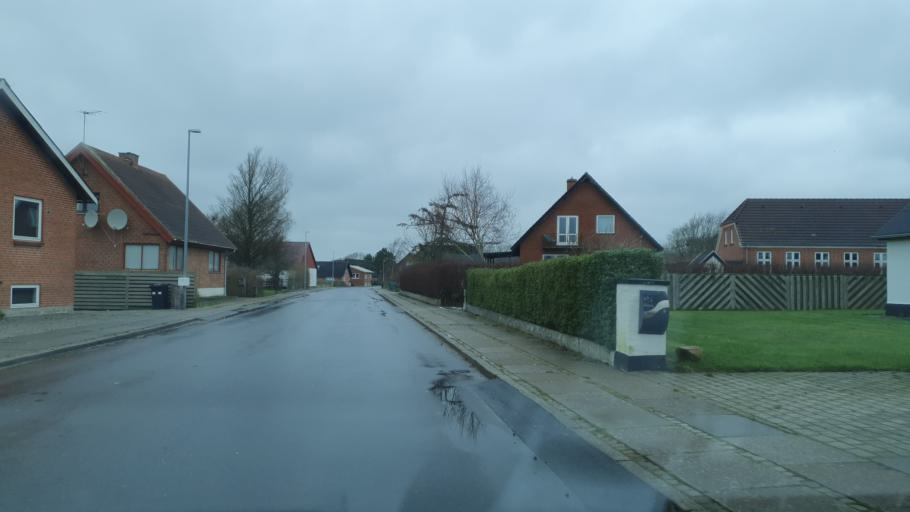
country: DK
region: North Denmark
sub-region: Jammerbugt Kommune
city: Fjerritslev
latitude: 57.1037
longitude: 9.1243
